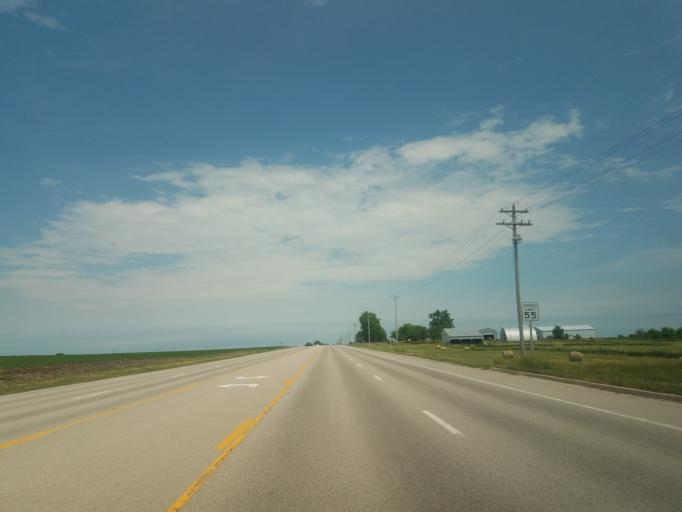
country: US
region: Illinois
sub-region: McLean County
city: Downs
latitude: 40.4262
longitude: -88.9012
